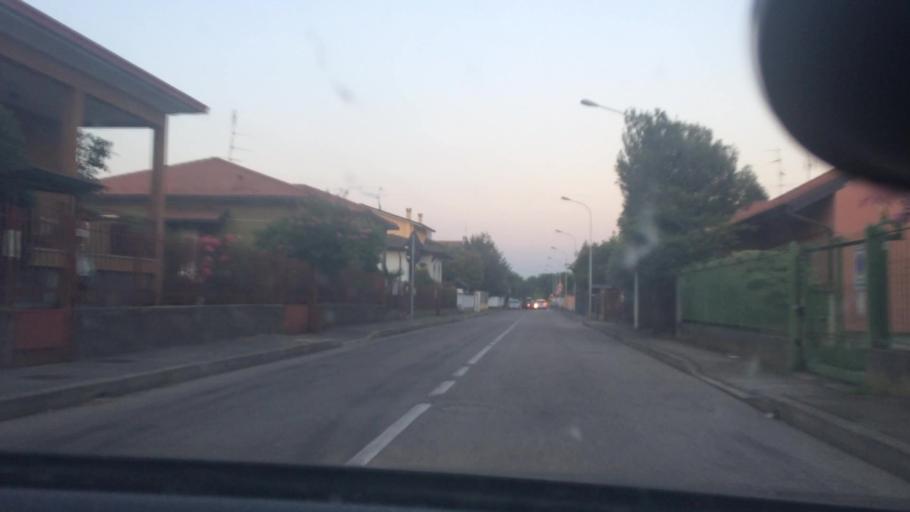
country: IT
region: Lombardy
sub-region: Citta metropolitana di Milano
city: Parabiago
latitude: 45.5455
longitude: 8.9422
